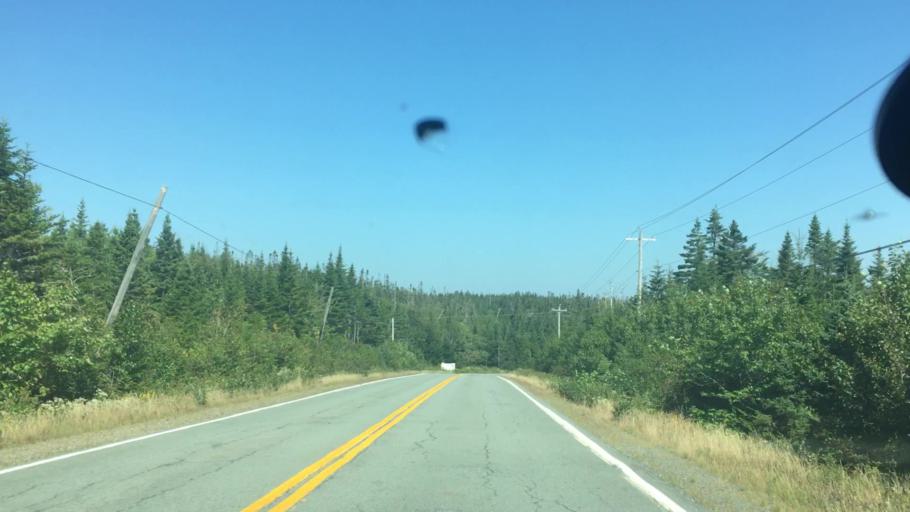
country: CA
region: Nova Scotia
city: Antigonish
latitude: 45.0114
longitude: -62.1054
